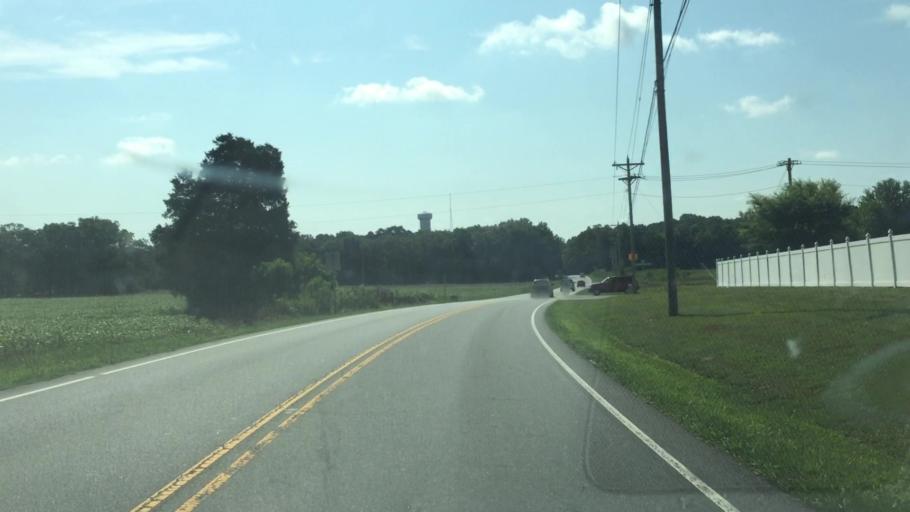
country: US
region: North Carolina
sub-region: Mecklenburg County
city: Mint Hill
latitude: 35.1682
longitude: -80.5979
